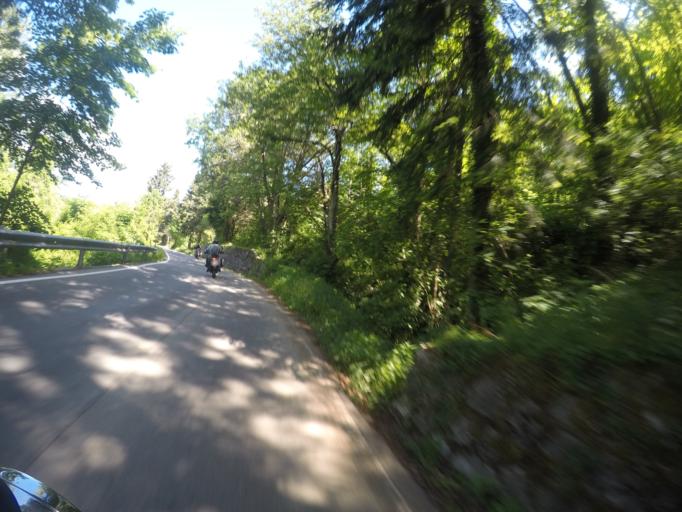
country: IT
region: Tuscany
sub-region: Provincia di Lucca
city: Careggine
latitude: 44.1081
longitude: 10.3334
